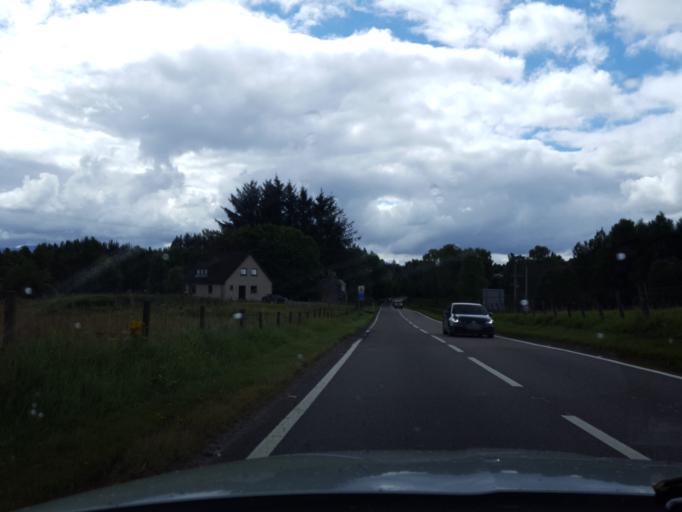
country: GB
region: Scotland
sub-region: Highland
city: Aviemore
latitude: 57.2450
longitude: -3.8041
